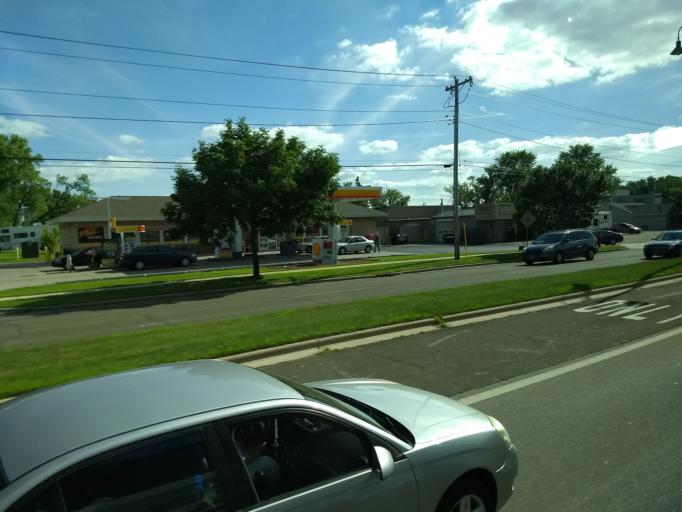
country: US
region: Wisconsin
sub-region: Dane County
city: Monona
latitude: 43.0482
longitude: -89.3120
